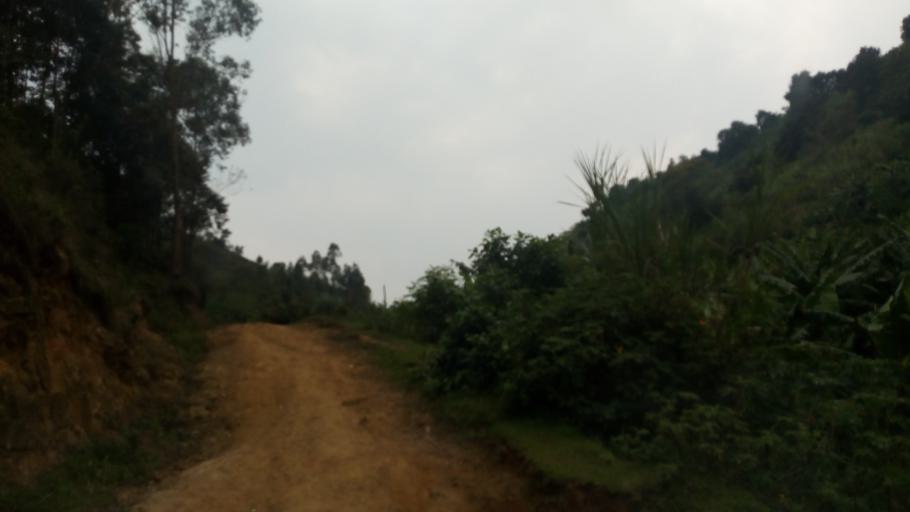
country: UG
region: Western Region
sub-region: Kisoro District
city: Kisoro
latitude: -1.2447
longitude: 29.6193
